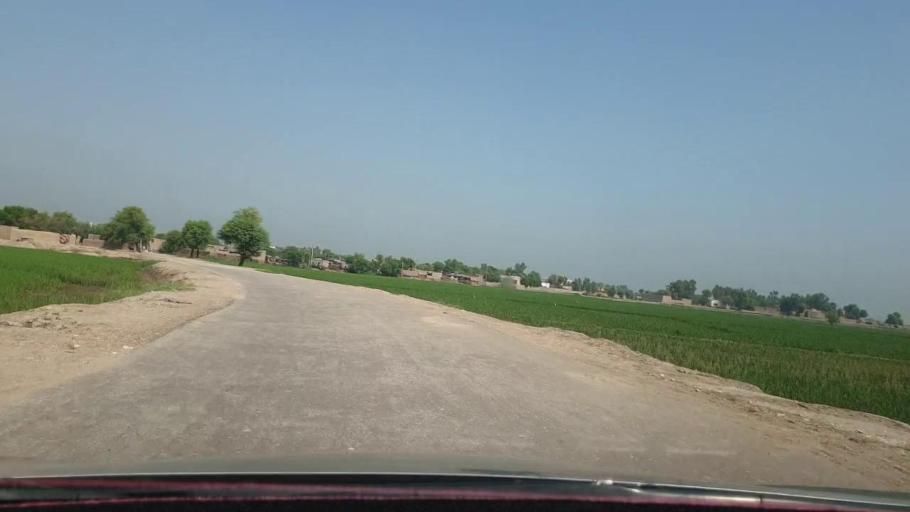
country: PK
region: Sindh
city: Warah
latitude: 27.4793
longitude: 67.8308
